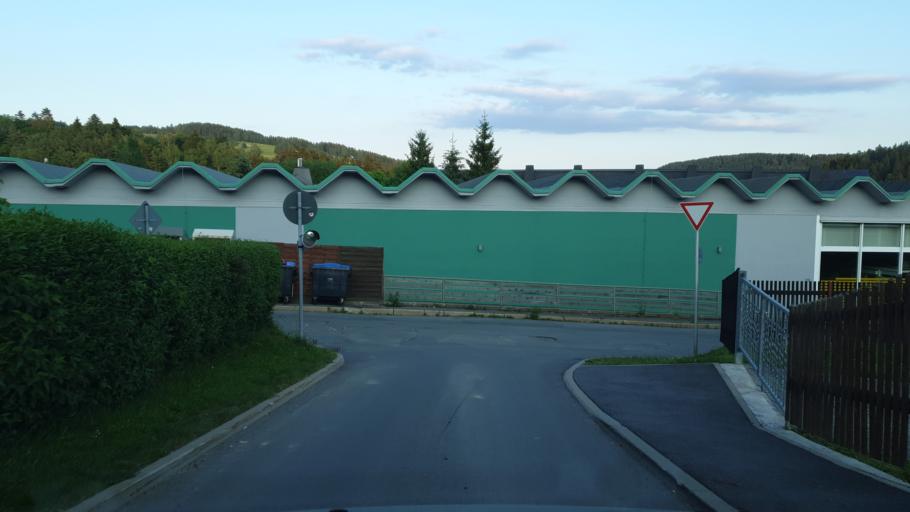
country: DE
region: Saxony
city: Klingenthal
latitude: 50.3602
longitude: 12.4573
